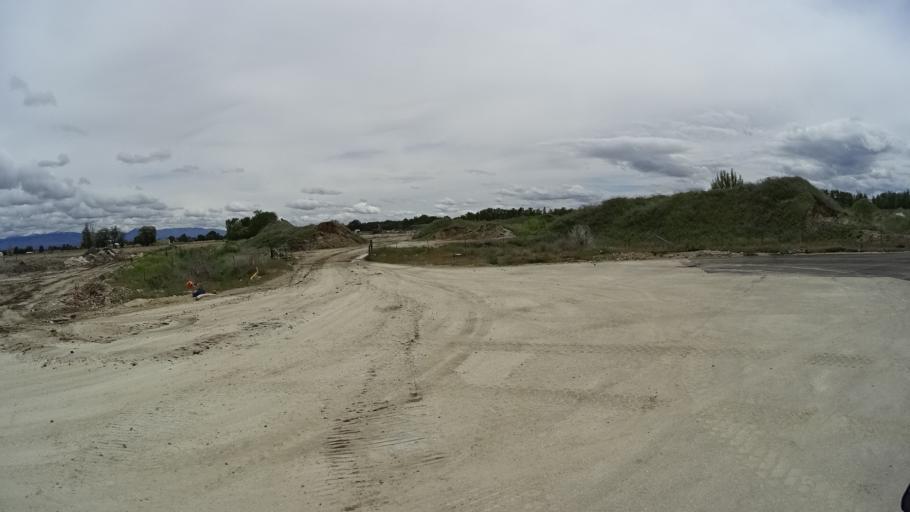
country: US
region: Idaho
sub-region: Ada County
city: Star
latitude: 43.6876
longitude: -116.4601
